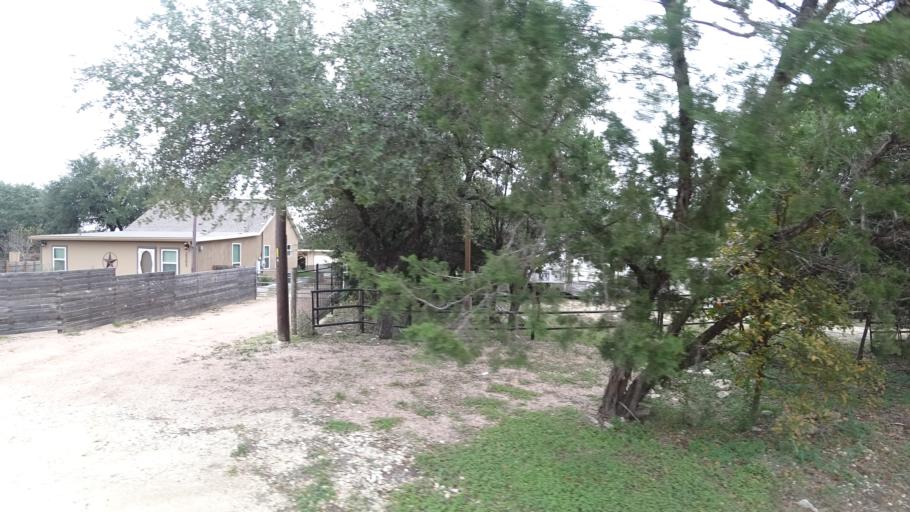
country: US
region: Texas
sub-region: Travis County
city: Hudson Bend
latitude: 30.3857
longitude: -97.9403
